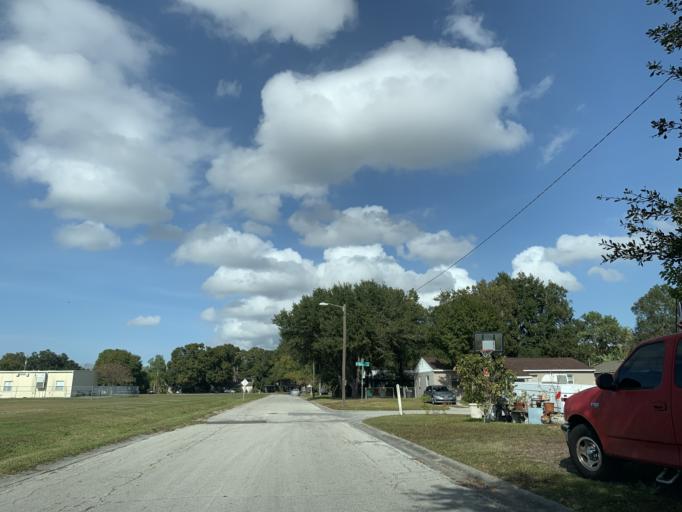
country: US
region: Florida
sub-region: Hillsborough County
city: Tampa
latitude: 27.9062
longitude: -82.5135
